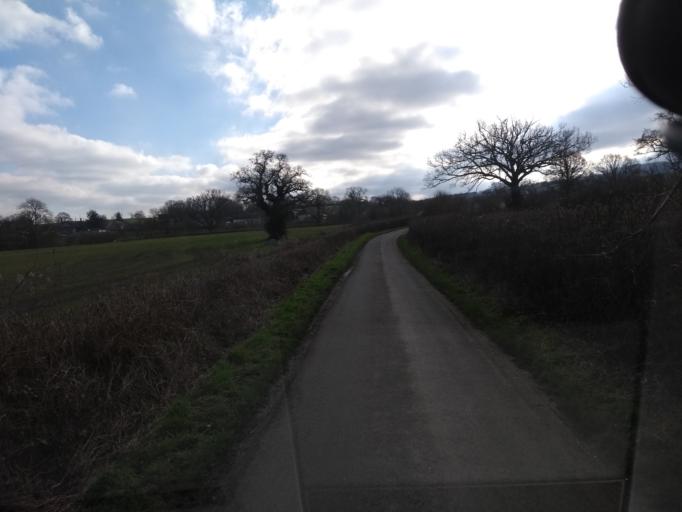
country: GB
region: England
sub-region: Somerset
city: Creech Saint Michael
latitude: 50.9582
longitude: -3.0321
